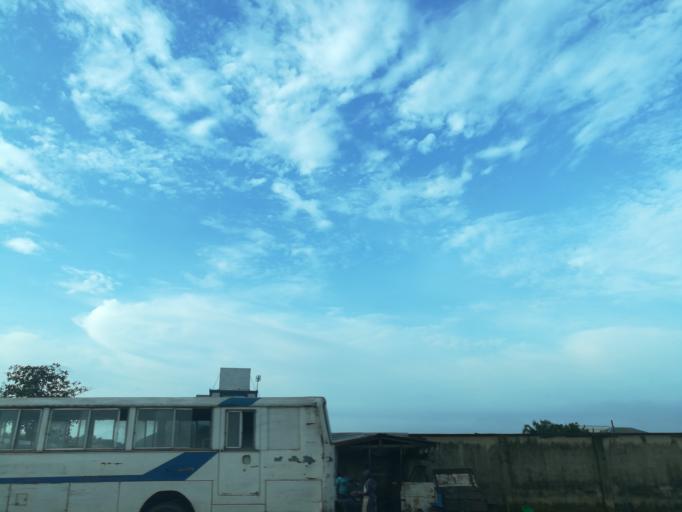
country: NG
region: Lagos
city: Ebute Ikorodu
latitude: 6.6194
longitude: 3.4653
